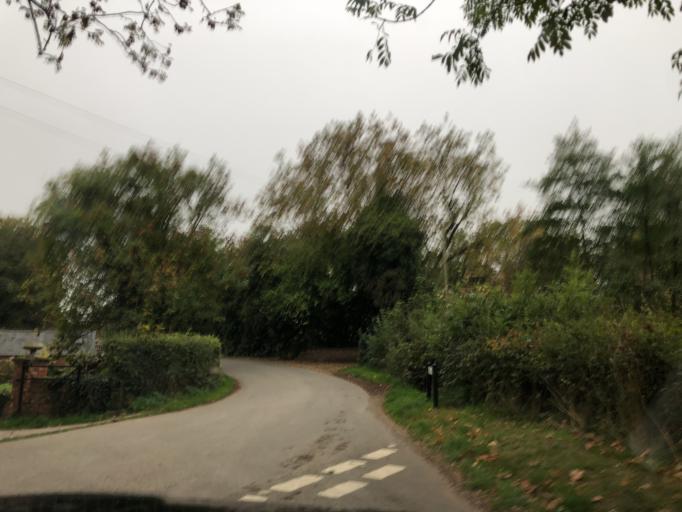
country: GB
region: England
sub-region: Warwickshire
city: Wroxall
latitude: 52.3142
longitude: -1.6567
